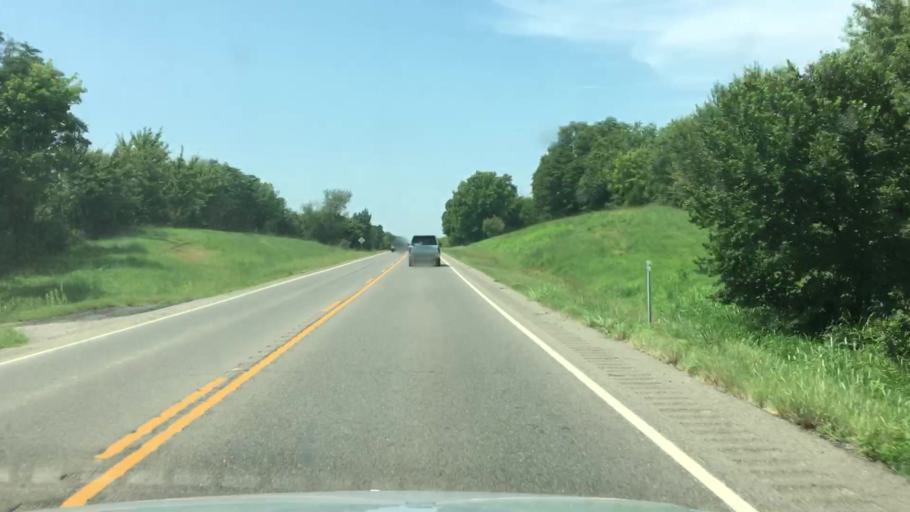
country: US
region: Oklahoma
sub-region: Wagoner County
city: Wagoner
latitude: 35.9371
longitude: -95.3383
